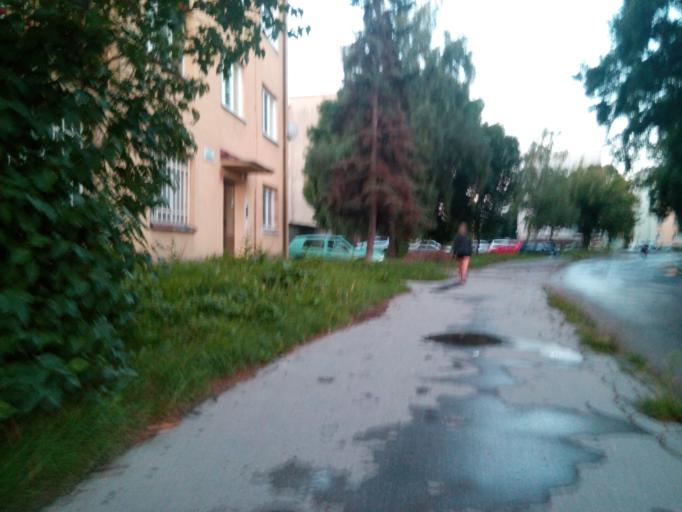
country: SK
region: Kosicky
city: Kosice
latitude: 48.7387
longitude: 21.2566
